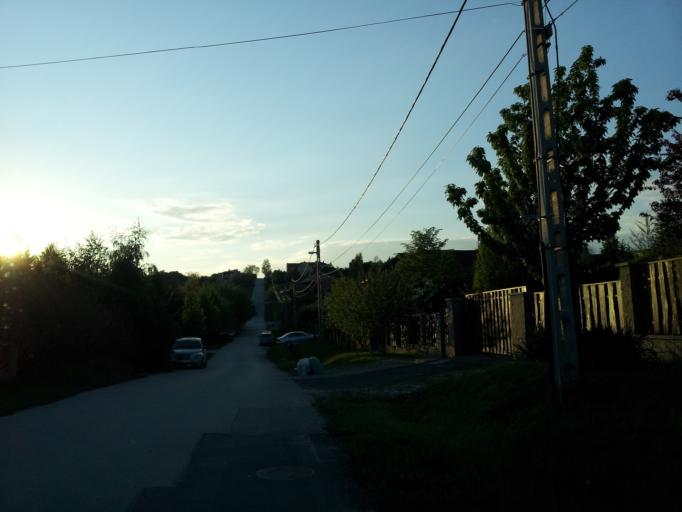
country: HU
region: Pest
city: Piliscsaba
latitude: 47.6198
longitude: 18.8195
